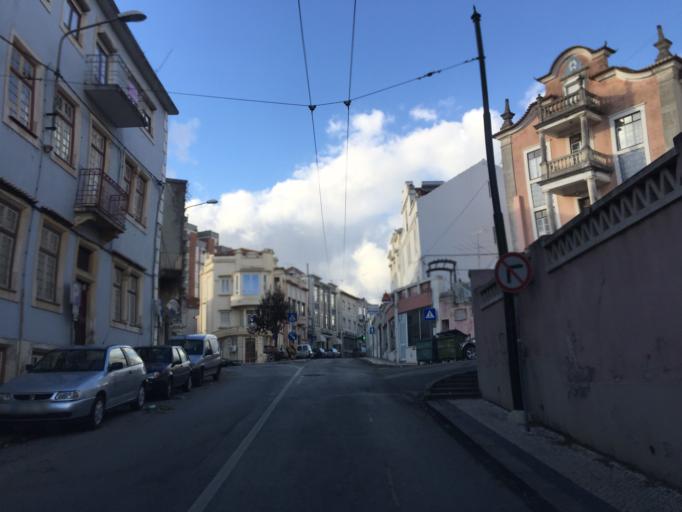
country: PT
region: Coimbra
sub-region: Coimbra
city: Coimbra
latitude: 40.2133
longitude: -8.4276
